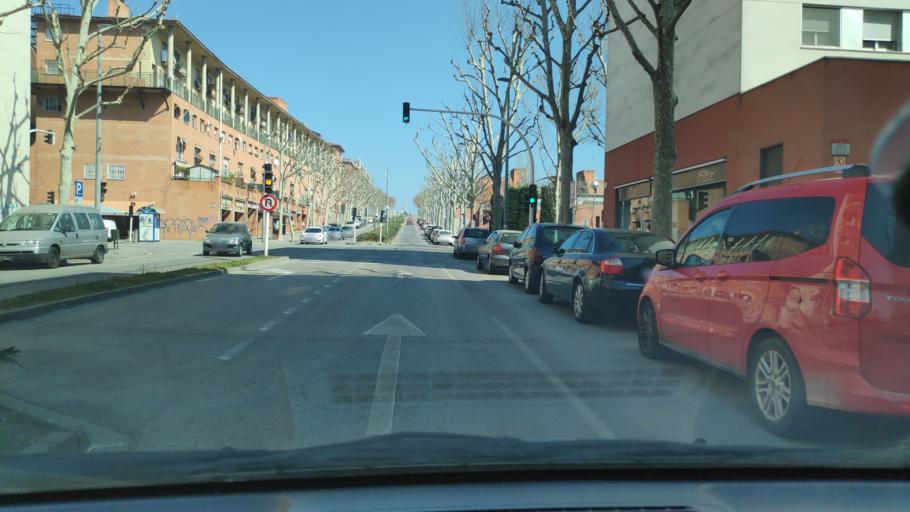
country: ES
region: Catalonia
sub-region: Provincia de Barcelona
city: Mollet del Valles
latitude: 41.5465
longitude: 2.2079
